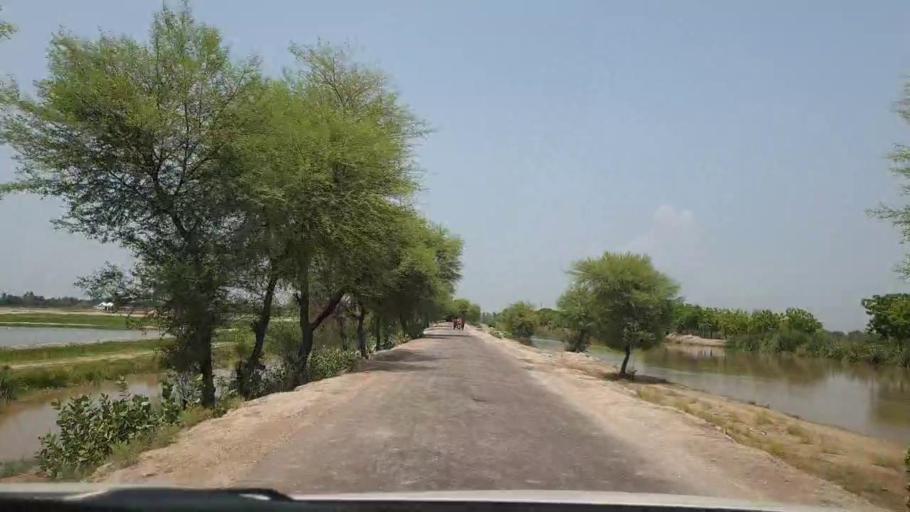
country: PK
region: Sindh
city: Dokri
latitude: 27.3554
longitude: 68.1130
